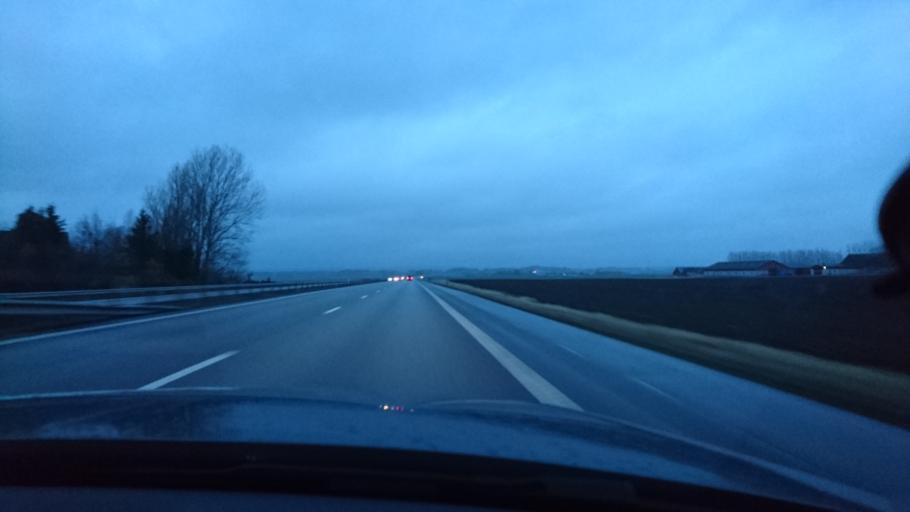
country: SE
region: Skane
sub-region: Astorps Kommun
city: Astorp
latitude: 56.1734
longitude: 12.9942
